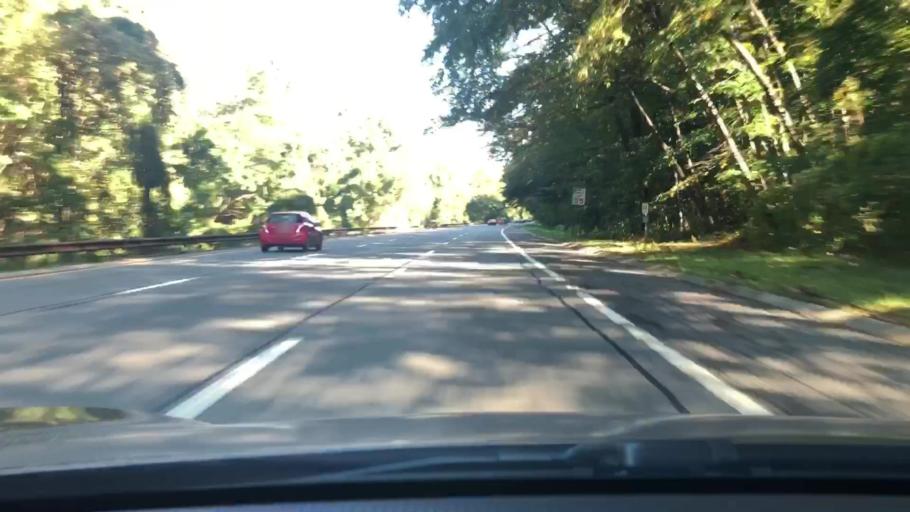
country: US
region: New York
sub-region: Westchester County
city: Greenville
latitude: 40.9931
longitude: -73.8371
